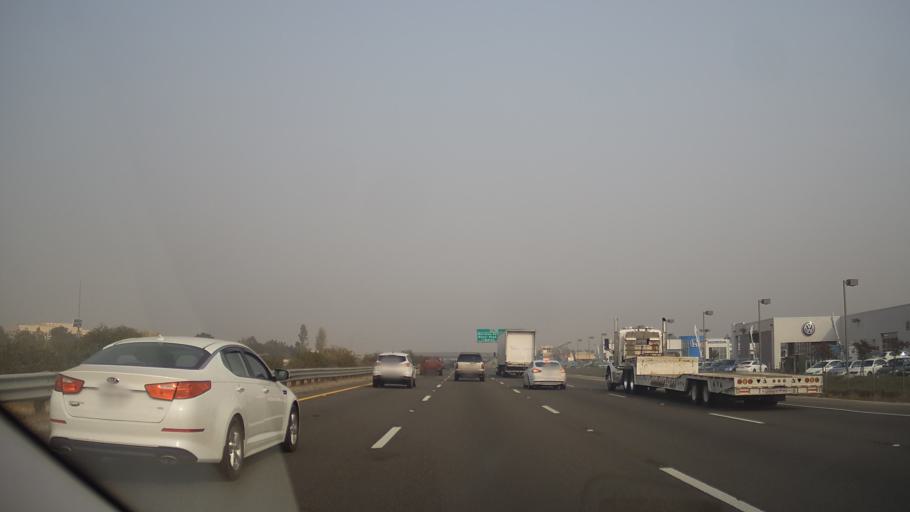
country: US
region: California
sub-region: Solano County
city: Hartley
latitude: 38.3847
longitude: -121.9398
